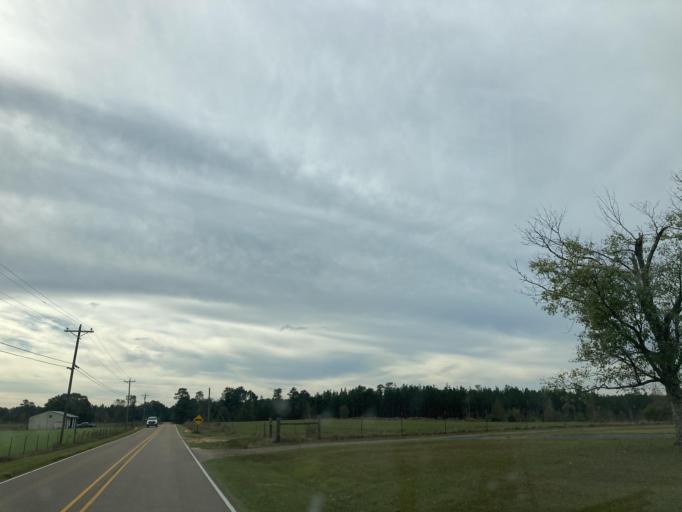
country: US
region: Mississippi
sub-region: Lamar County
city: Purvis
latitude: 31.1046
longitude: -89.4718
